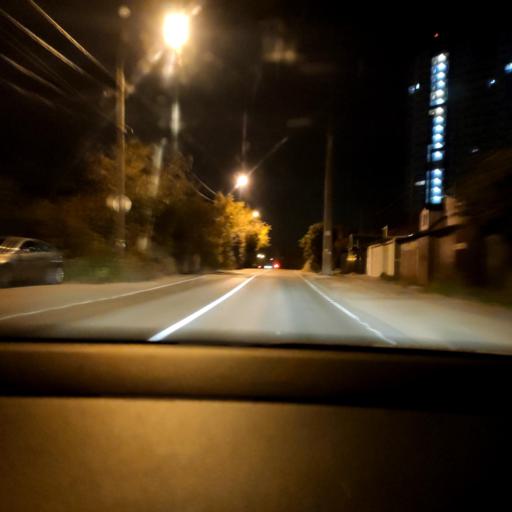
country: RU
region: Moskovskaya
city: Bolshevo
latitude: 55.9459
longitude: 37.8318
